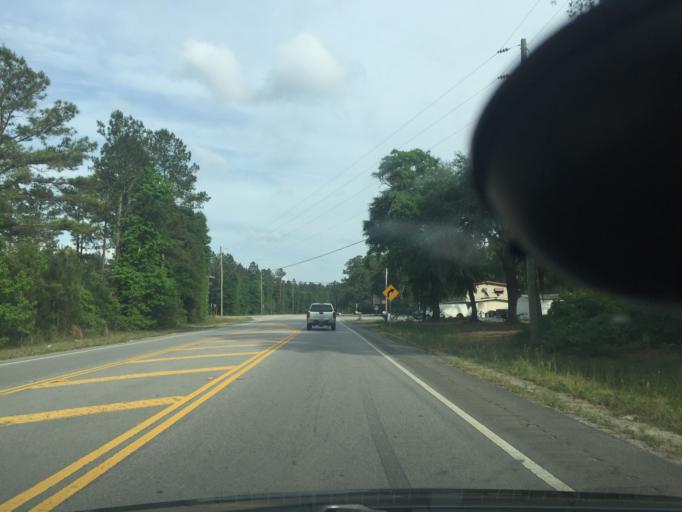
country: US
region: Georgia
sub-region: Chatham County
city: Bloomingdale
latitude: 32.0739
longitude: -81.3634
